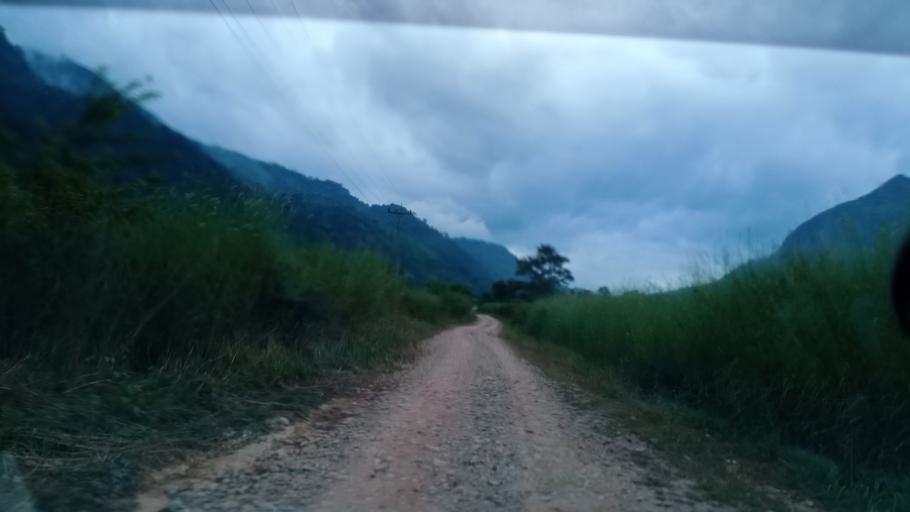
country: TH
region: Changwat Bueng Kan
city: Pak Khat
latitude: 18.7243
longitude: 103.2385
